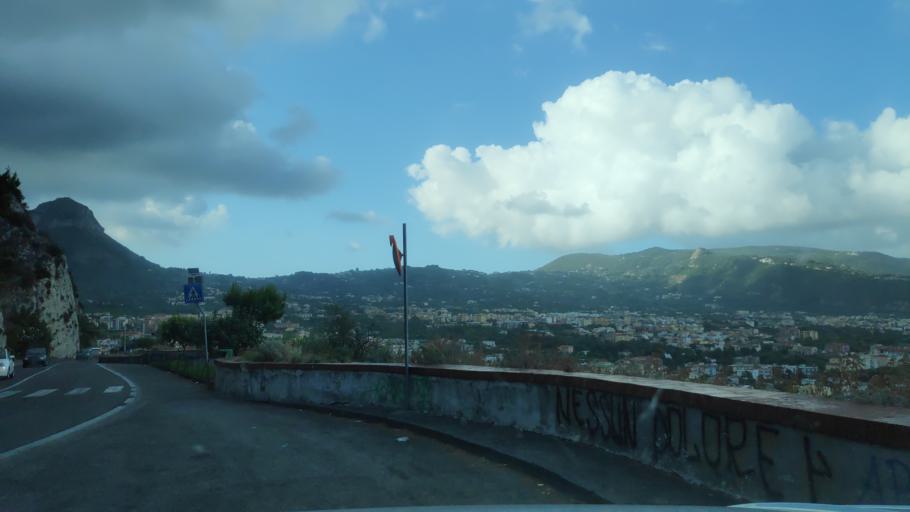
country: IT
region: Campania
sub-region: Provincia di Napoli
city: Meta
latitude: 40.6478
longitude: 14.4121
